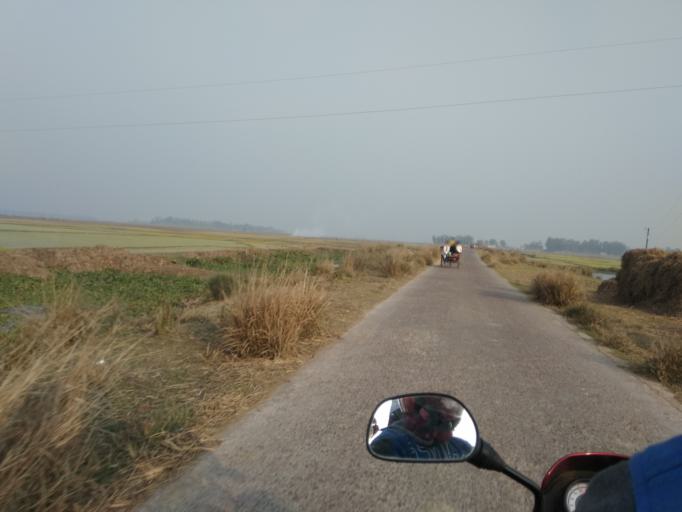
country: BD
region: Rajshahi
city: Ishurdi
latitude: 24.4953
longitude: 89.1908
